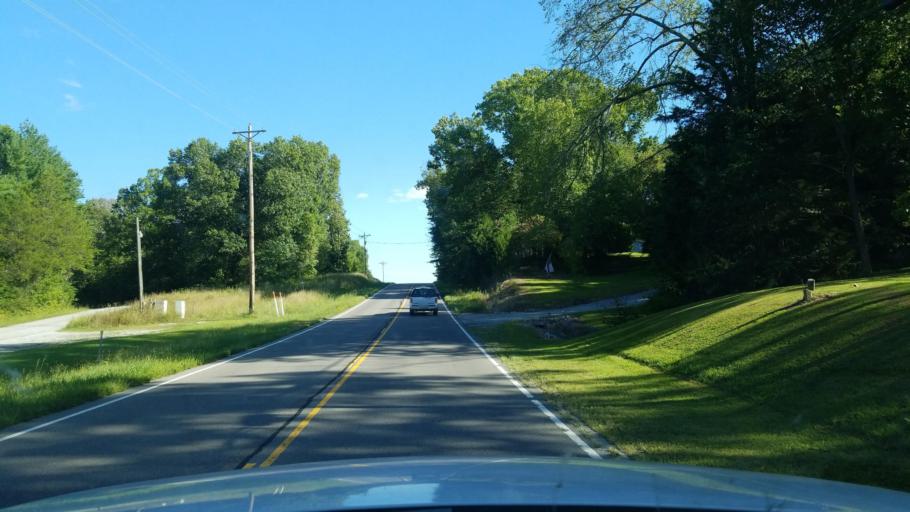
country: US
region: Illinois
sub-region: Saline County
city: Harrisburg
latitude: 37.6226
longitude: -88.4728
